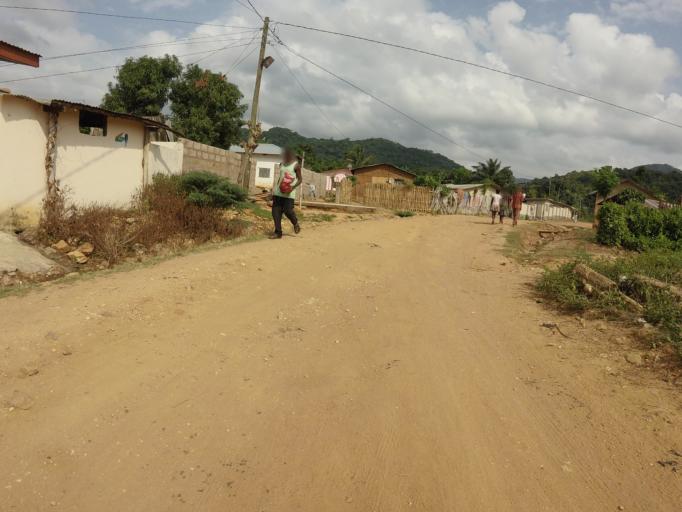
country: GH
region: Volta
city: Kpandu
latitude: 6.8938
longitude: 0.4333
